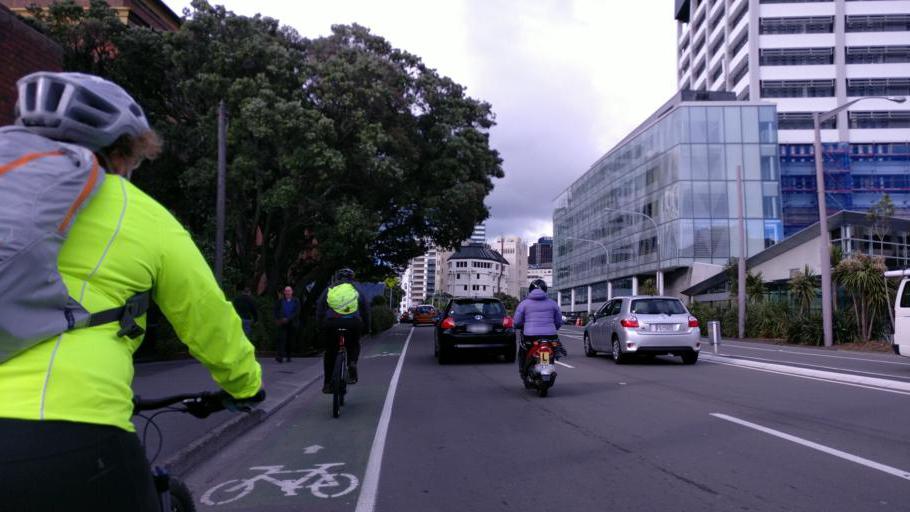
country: NZ
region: Wellington
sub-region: Wellington City
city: Wellington
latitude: -41.2782
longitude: 174.7802
